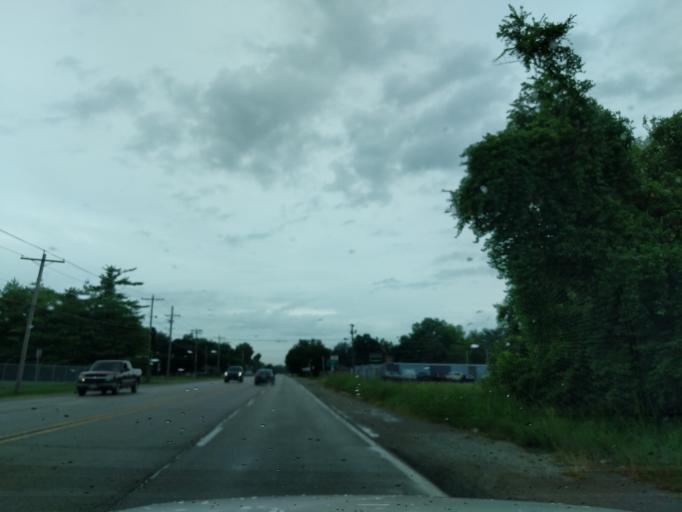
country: US
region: Illinois
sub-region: Saint Clair County
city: Fairmont City
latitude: 38.6593
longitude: -90.0819
